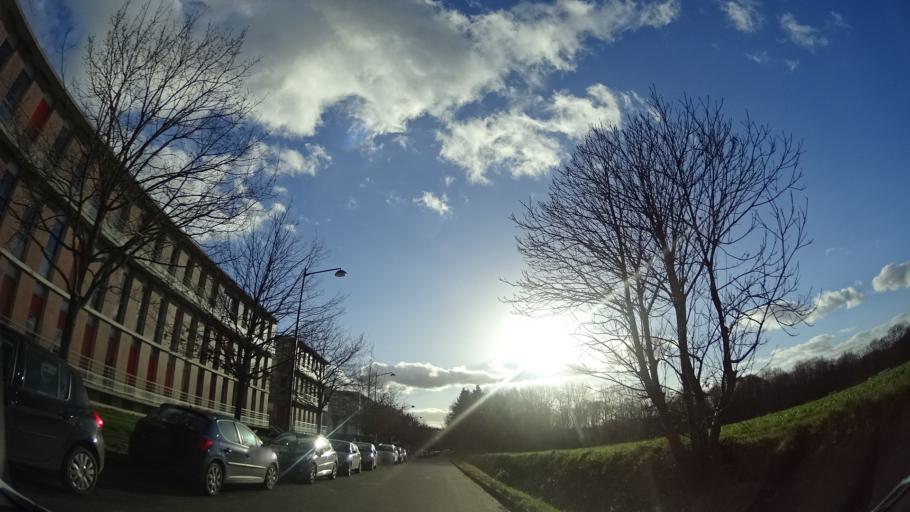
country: FR
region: Brittany
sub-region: Departement d'Ille-et-Vilaine
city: Cesson-Sevigne
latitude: 48.1344
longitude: -1.6378
